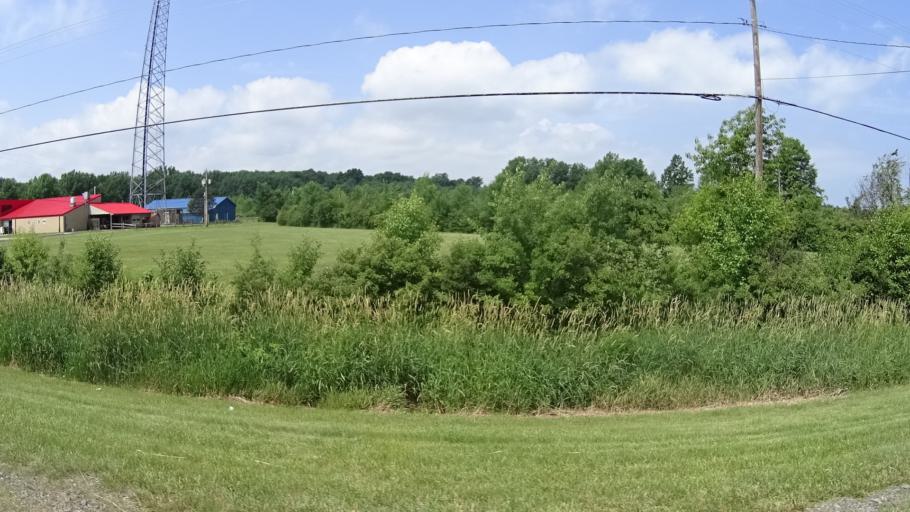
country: US
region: Ohio
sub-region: Lorain County
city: Vermilion
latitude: 41.3911
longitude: -82.3646
